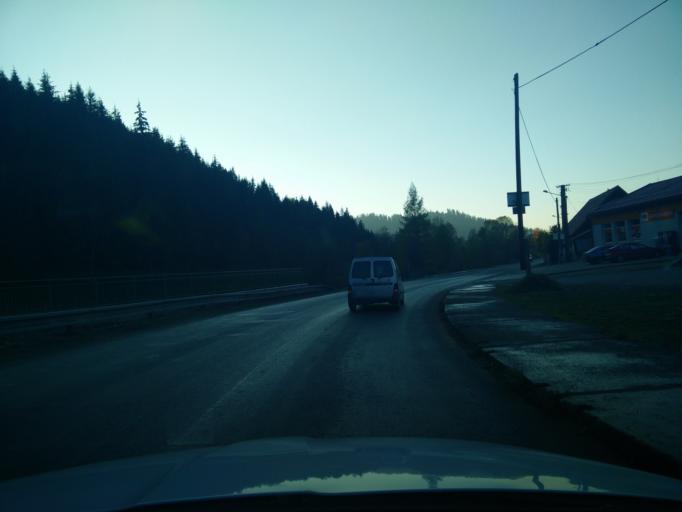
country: SK
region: Zilinsky
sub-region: Okres Zilina
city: Terchova
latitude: 49.3439
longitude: 19.0061
